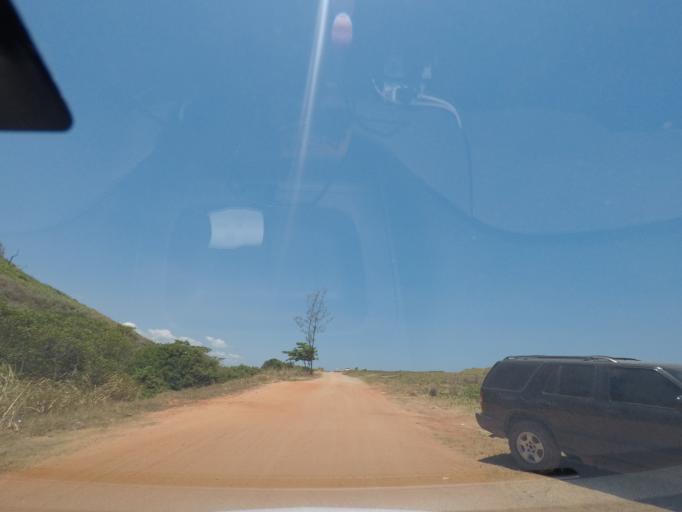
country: BR
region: Rio de Janeiro
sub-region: Niteroi
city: Niteroi
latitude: -22.9689
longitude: -43.0019
